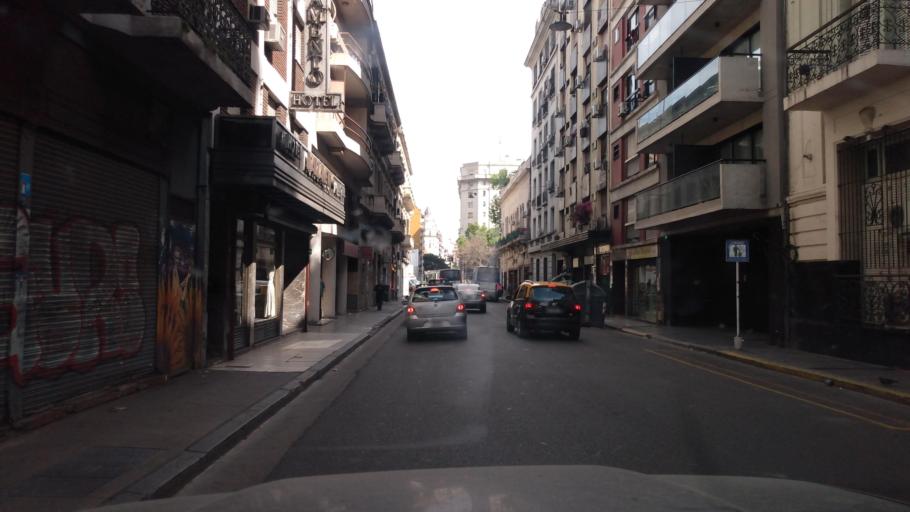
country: AR
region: Buenos Aires F.D.
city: Buenos Aires
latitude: -34.6082
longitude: -58.3907
